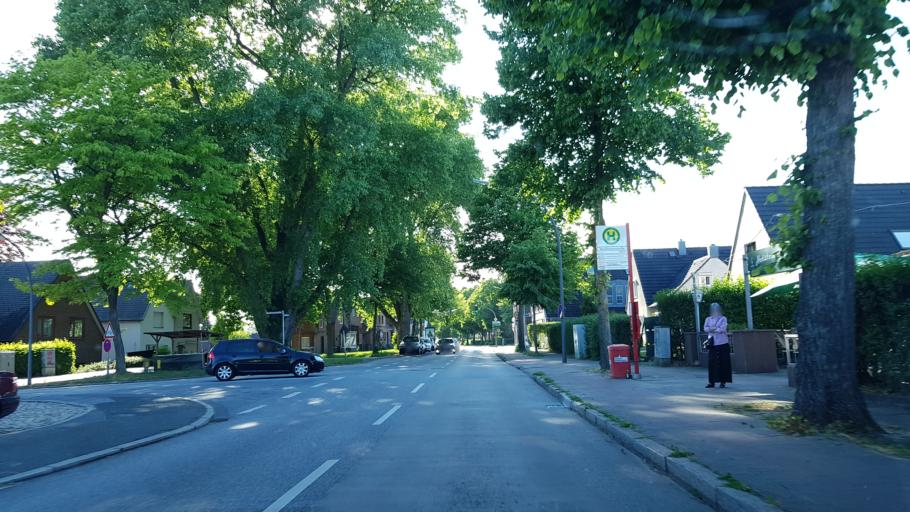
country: DE
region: Hamburg
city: Altona
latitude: 53.5347
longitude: 9.8597
